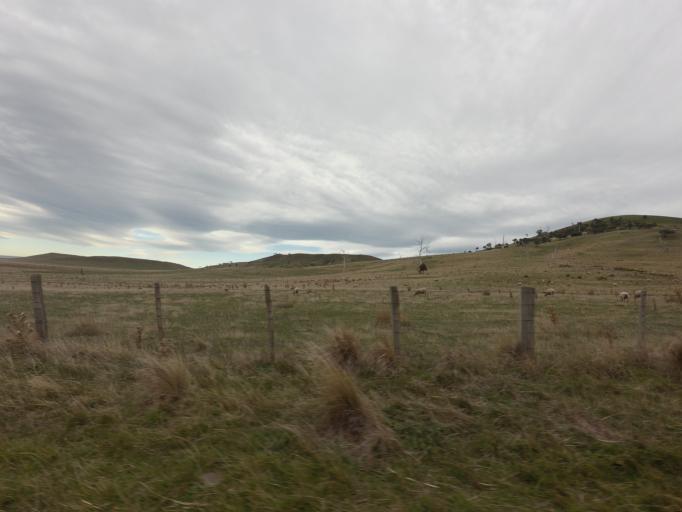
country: AU
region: Tasmania
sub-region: Derwent Valley
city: New Norfolk
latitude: -42.3783
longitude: 146.8659
